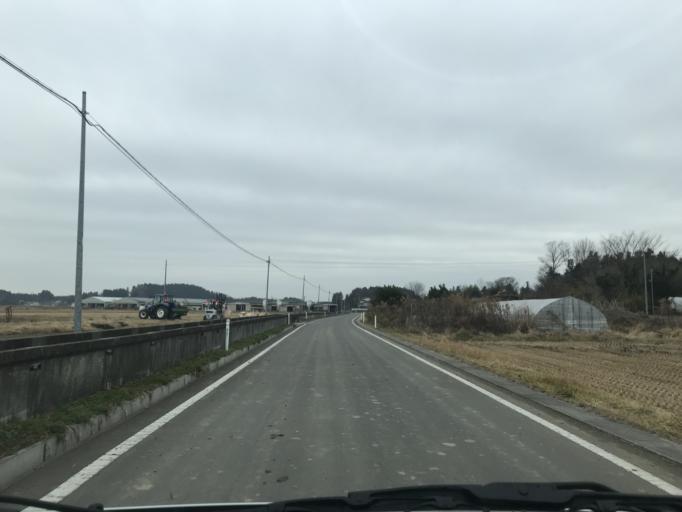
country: JP
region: Iwate
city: Ichinoseki
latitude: 38.7383
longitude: 141.2260
